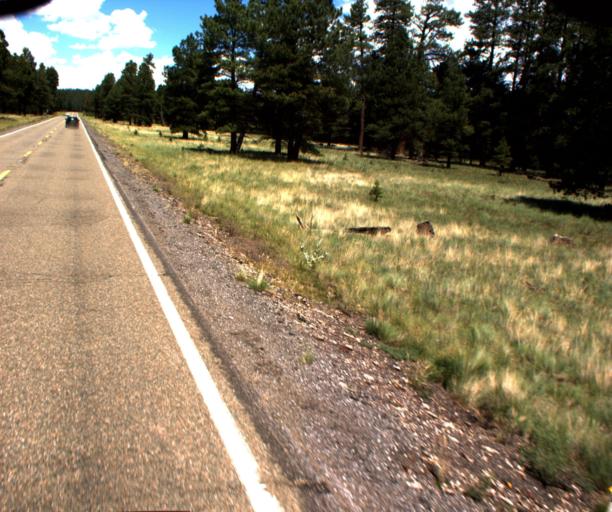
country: US
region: Arizona
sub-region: Coconino County
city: Parks
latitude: 35.3680
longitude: -111.7908
